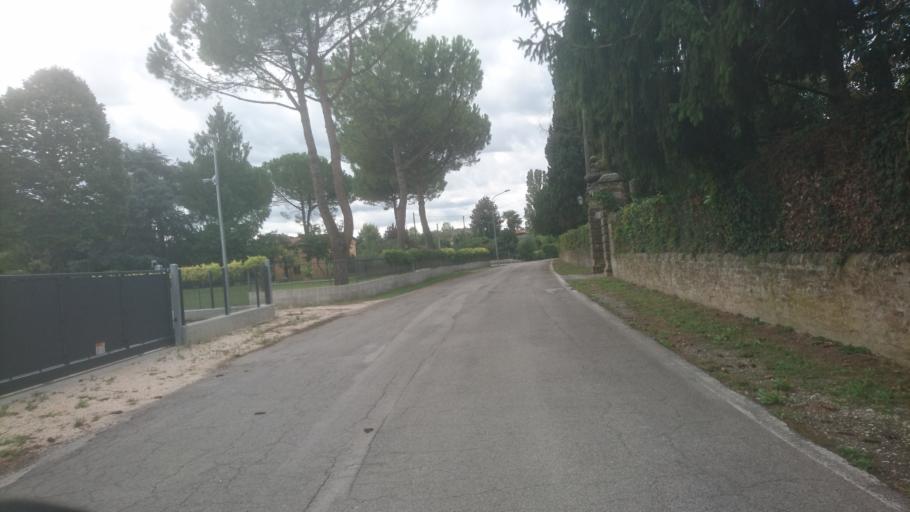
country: IT
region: Veneto
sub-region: Provincia di Venezia
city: Vigonovo
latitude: 45.3947
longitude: 12.0004
